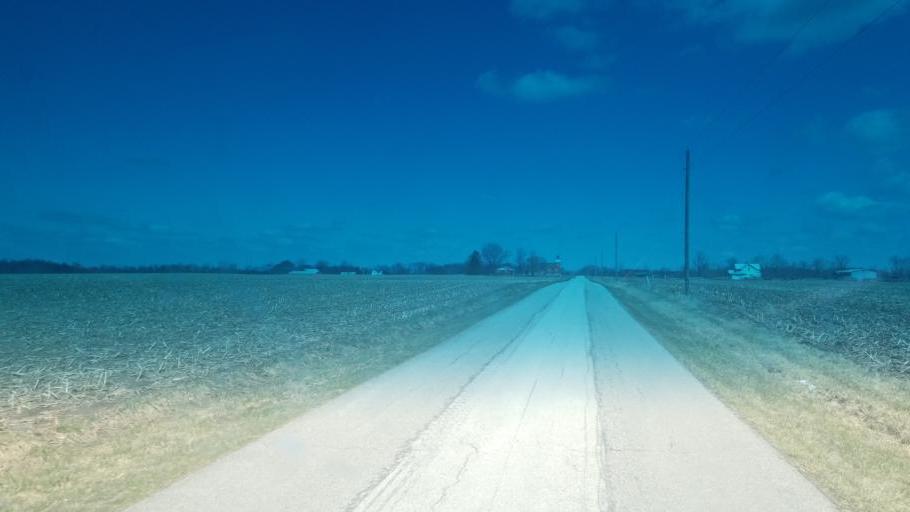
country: US
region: Ohio
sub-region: Crawford County
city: Bucyrus
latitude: 40.8069
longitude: -83.0738
